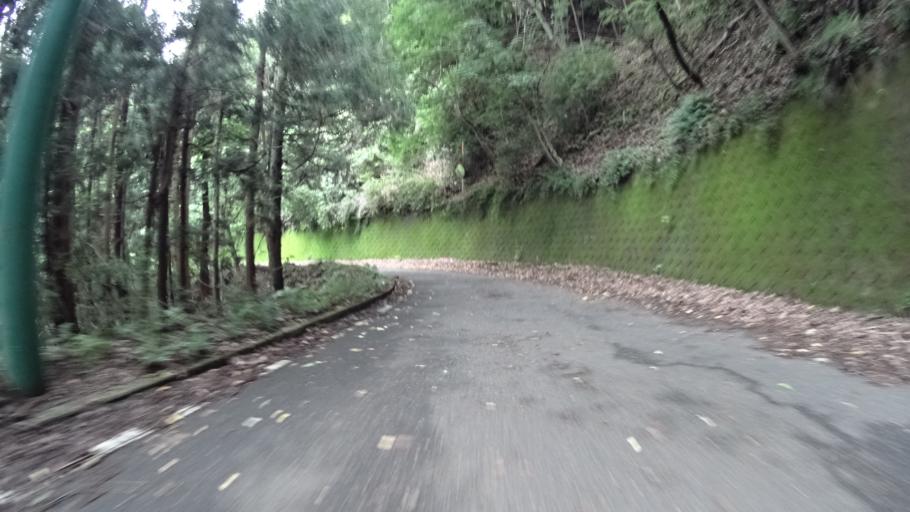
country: JP
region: Kanagawa
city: Atsugi
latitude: 35.4999
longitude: 139.2675
